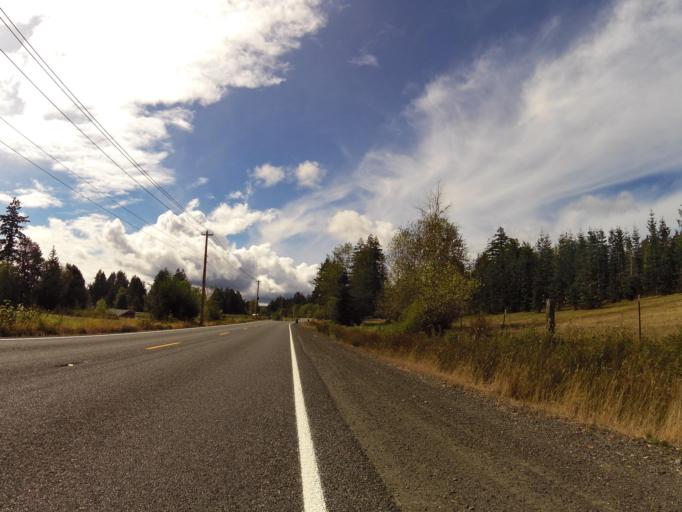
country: US
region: Washington
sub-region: Mason County
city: Shelton
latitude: 47.1545
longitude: -123.0556
